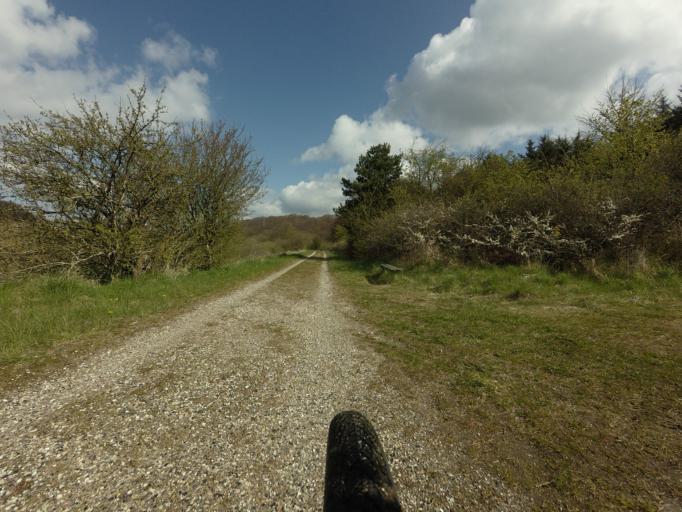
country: DK
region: North Denmark
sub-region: Mariagerfjord Kommune
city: Hadsund
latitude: 56.6842
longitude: 10.1052
